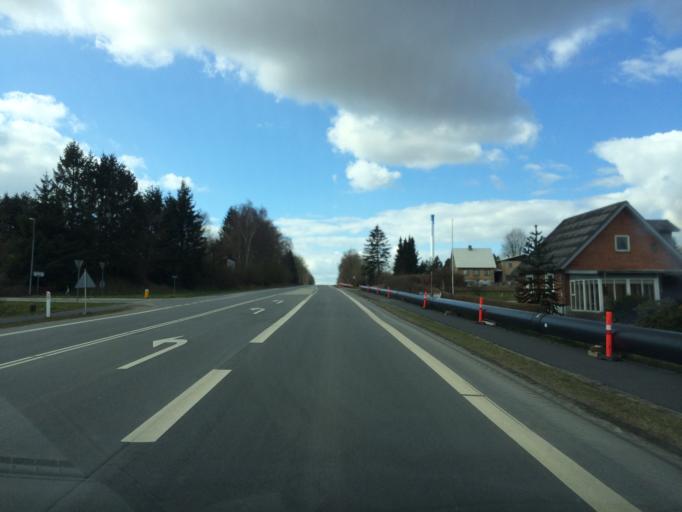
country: DK
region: South Denmark
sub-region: Assens Kommune
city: Vissenbjerg
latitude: 55.3880
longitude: 10.1497
